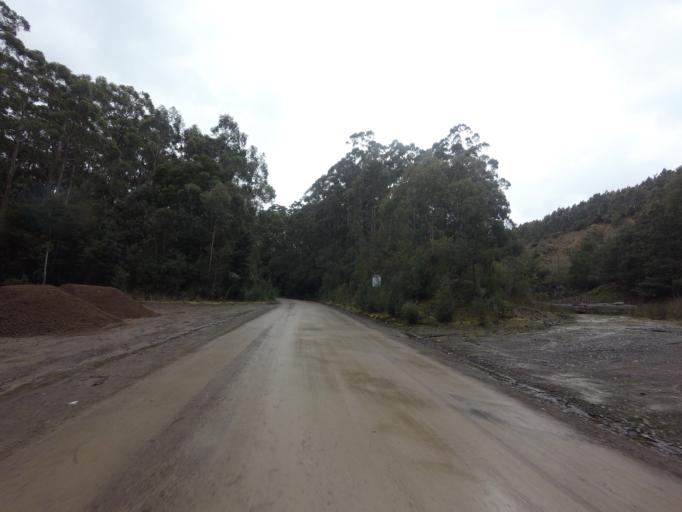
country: AU
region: Tasmania
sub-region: Huon Valley
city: Geeveston
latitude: -43.4997
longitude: 146.8786
